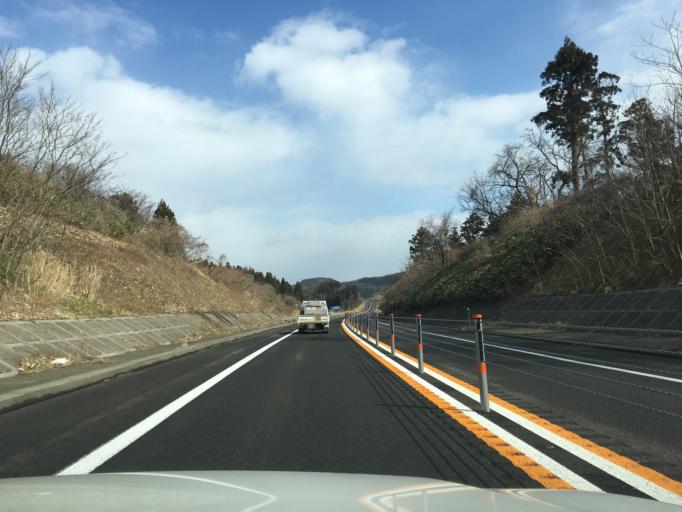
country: JP
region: Akita
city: Akita Shi
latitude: 39.4835
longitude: 140.0533
